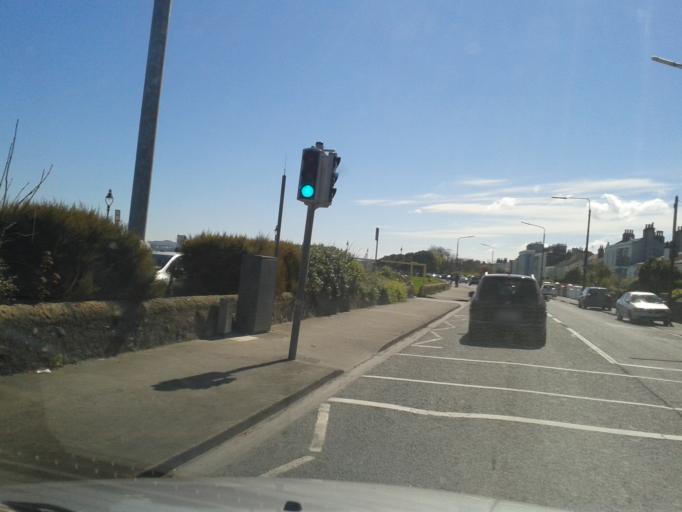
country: IE
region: Leinster
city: Sandymount
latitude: 53.3281
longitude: -6.2087
